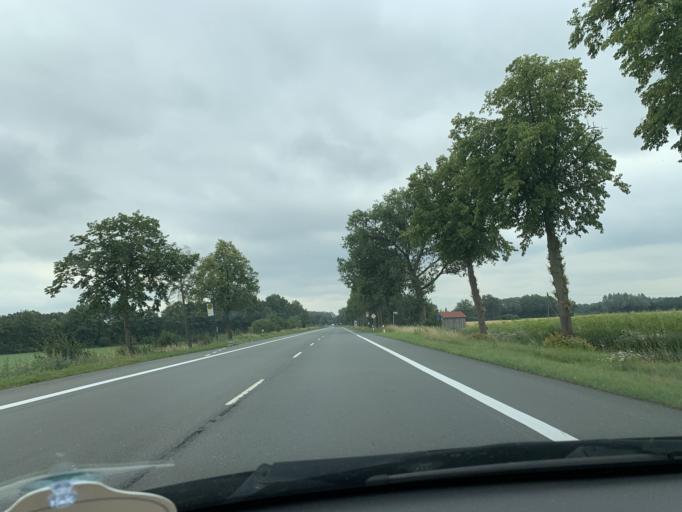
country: DE
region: North Rhine-Westphalia
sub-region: Regierungsbezirk Munster
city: Ennigerloh
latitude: 51.9084
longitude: 8.0479
